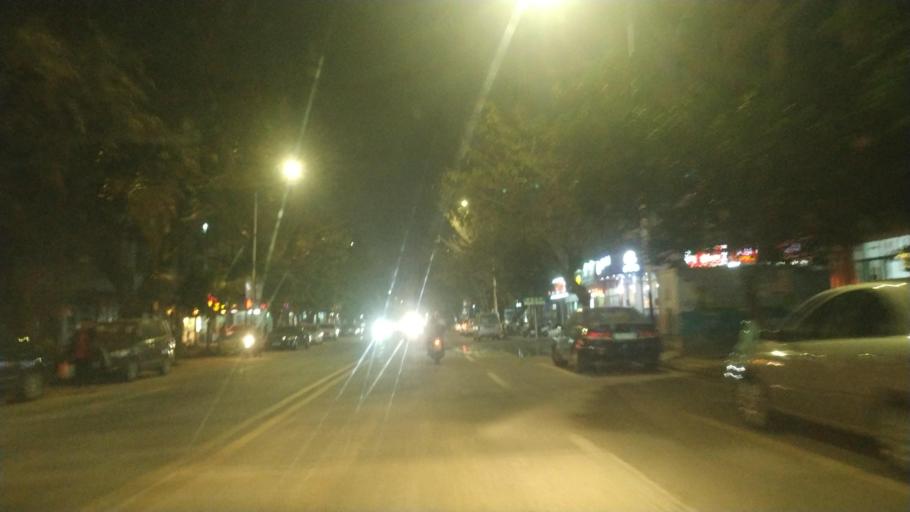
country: CN
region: Guangdong
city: Xiaguo
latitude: 21.6444
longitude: 110.6314
